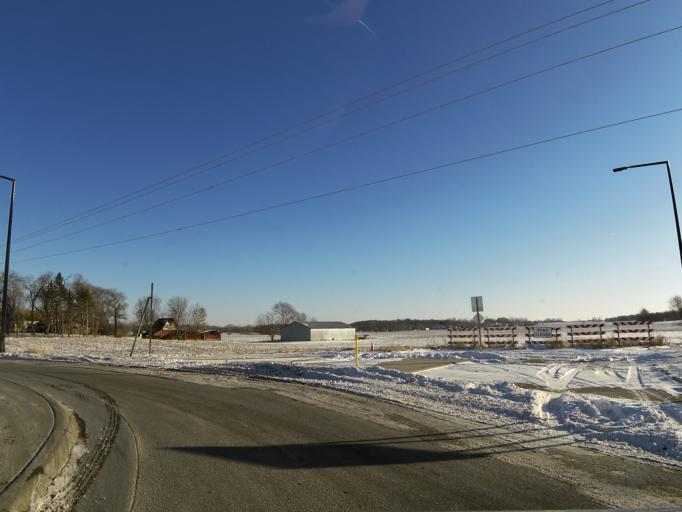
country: US
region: Minnesota
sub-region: Le Sueur County
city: New Prague
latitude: 44.5436
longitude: -93.5975
